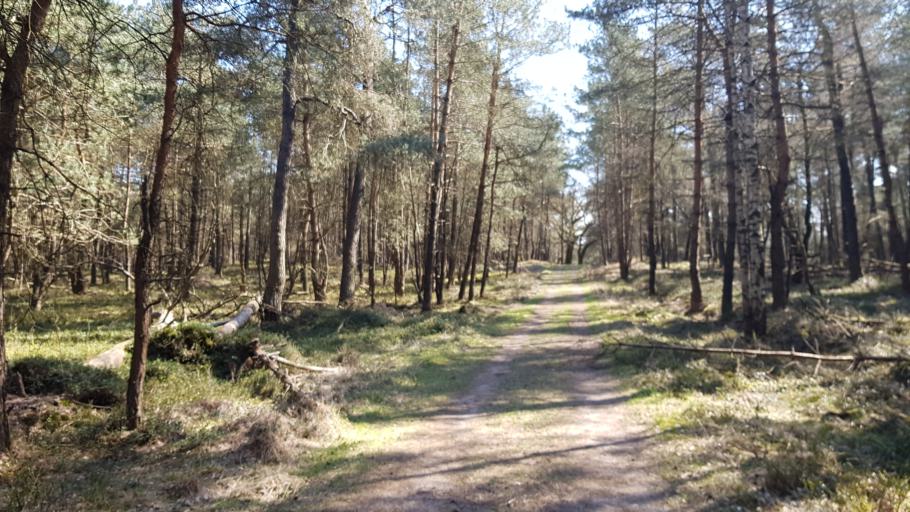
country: NL
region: Gelderland
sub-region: Gemeente Rozendaal
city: Rozendaal
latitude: 52.0704
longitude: 5.9591
